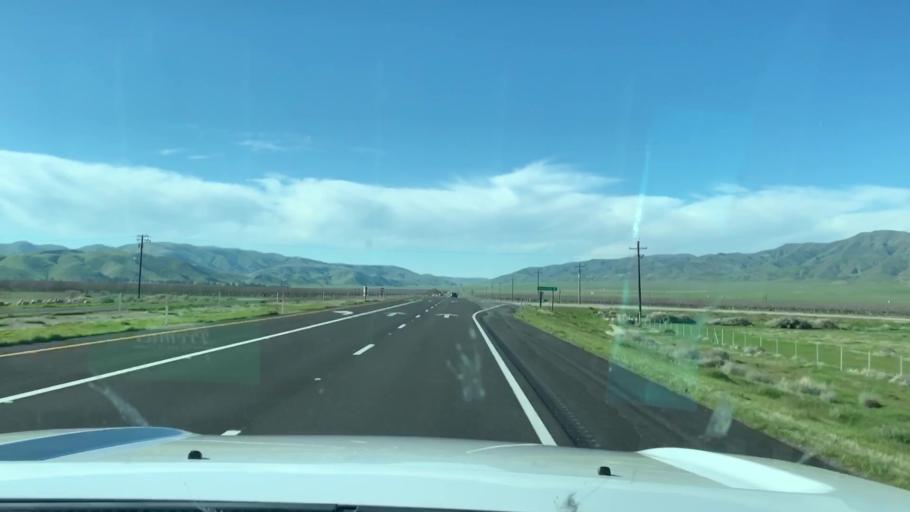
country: US
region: California
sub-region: San Luis Obispo County
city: Shandon
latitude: 35.6707
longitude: -120.0806
